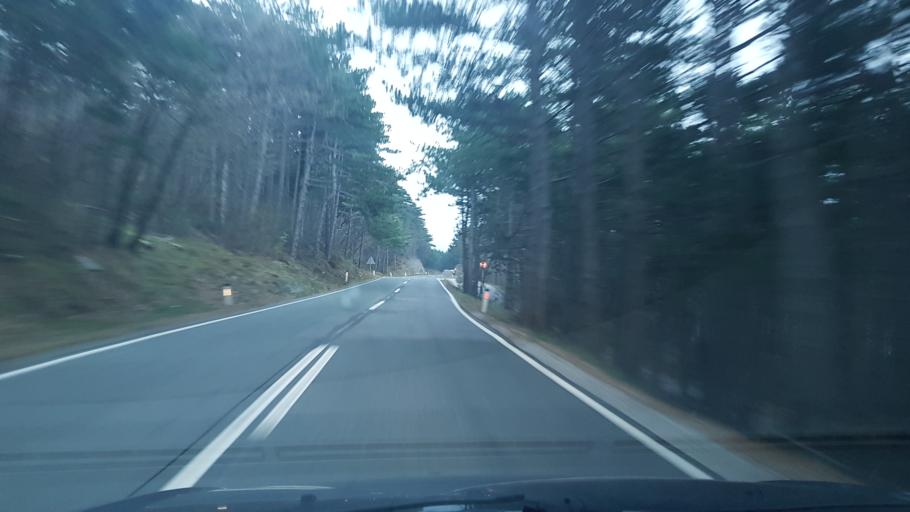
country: SI
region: Vipava
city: Vipava
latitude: 45.8807
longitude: 13.9517
